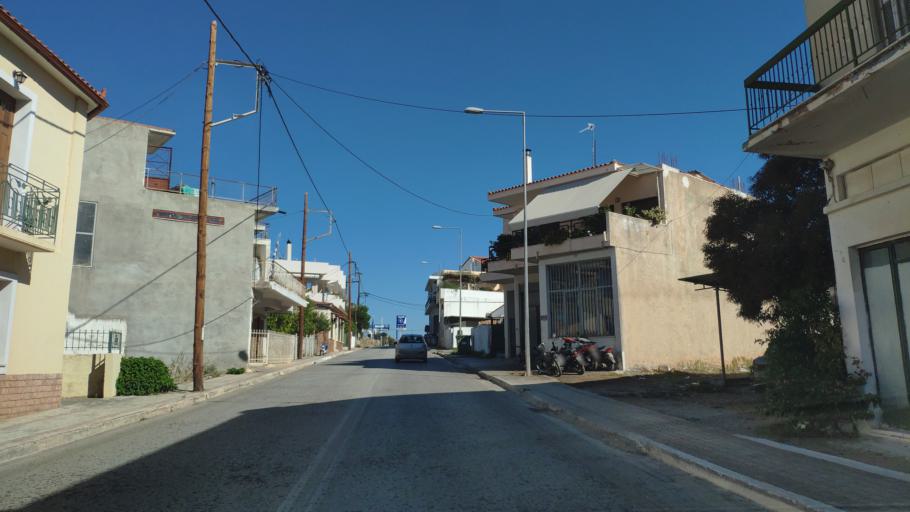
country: GR
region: Peloponnese
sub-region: Nomos Korinthias
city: Khiliomodhi
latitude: 37.8107
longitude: 22.8685
